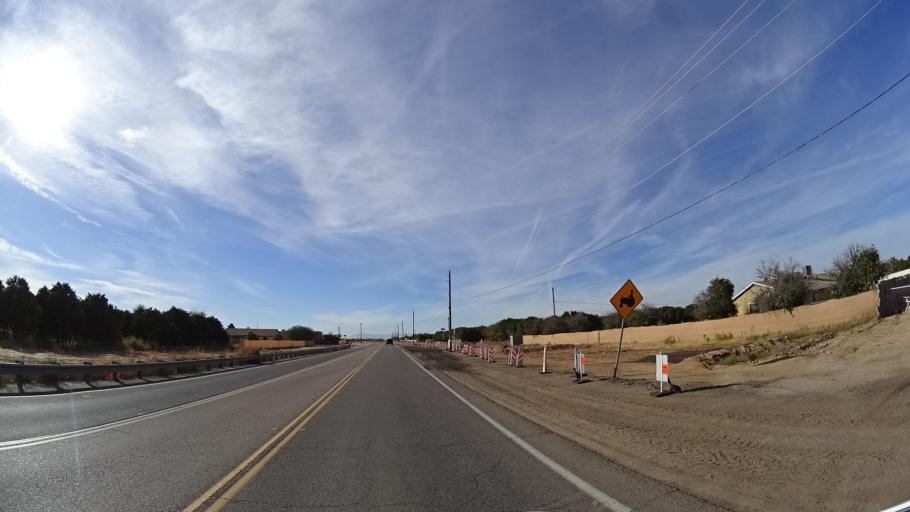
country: US
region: Arizona
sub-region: Maricopa County
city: Queen Creek
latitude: 33.2195
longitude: -111.6872
